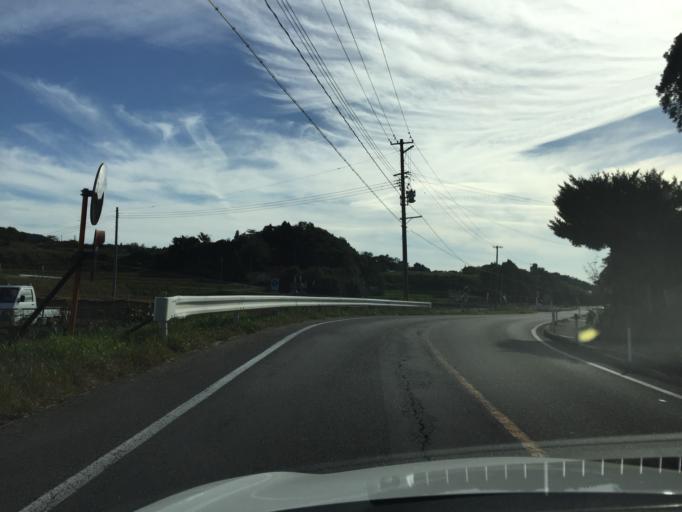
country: JP
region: Fukushima
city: Miharu
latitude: 37.4028
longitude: 140.4569
